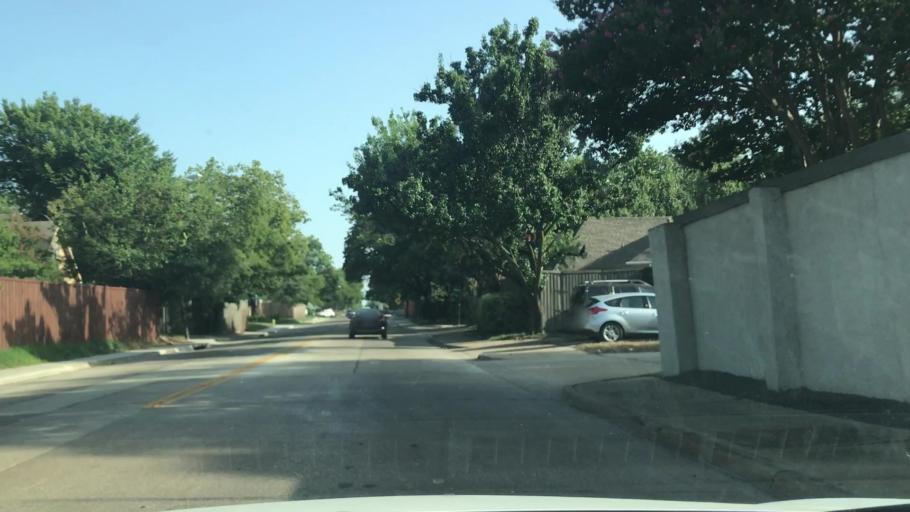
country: US
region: Texas
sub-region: Dallas County
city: Highland Park
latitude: 32.8280
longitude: -96.7702
